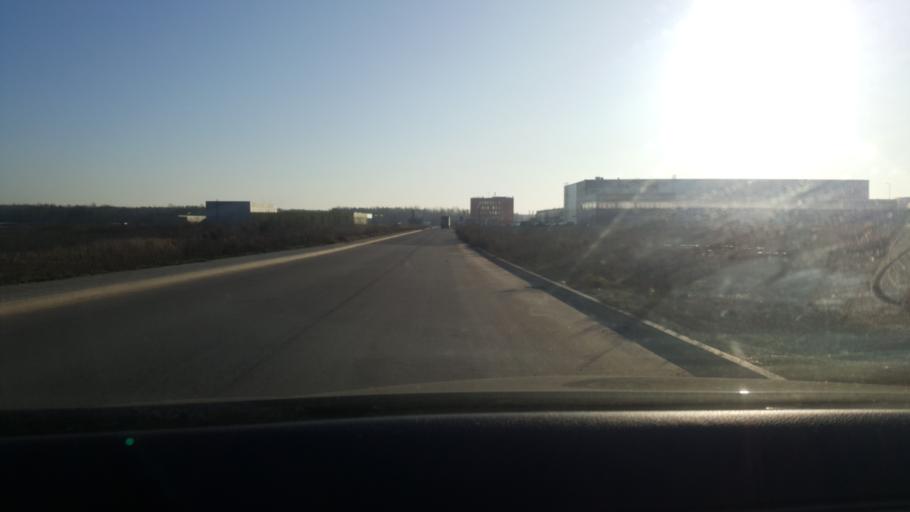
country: LT
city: Ramuciai
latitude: 54.9328
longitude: 24.0349
